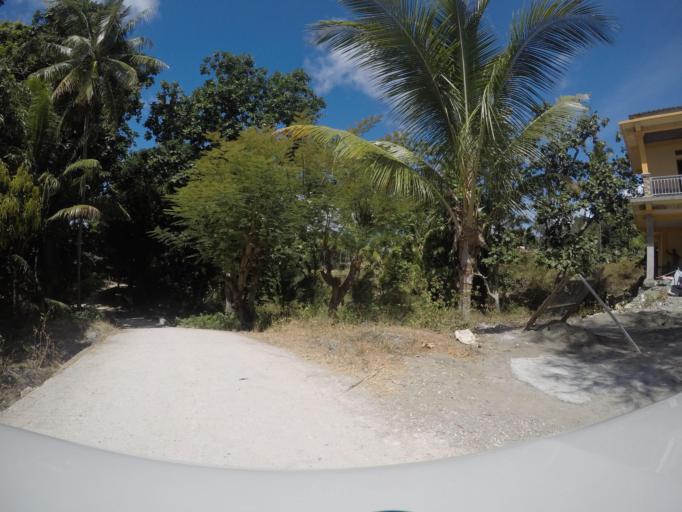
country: TL
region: Baucau
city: Baucau
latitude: -8.4553
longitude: 126.4456
